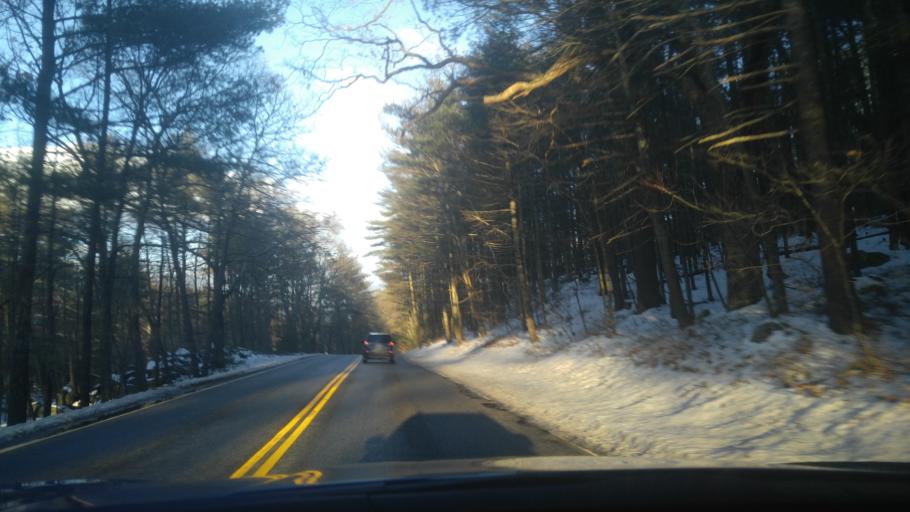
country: US
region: Rhode Island
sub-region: Kent County
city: Coventry
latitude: 41.7018
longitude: -71.6328
